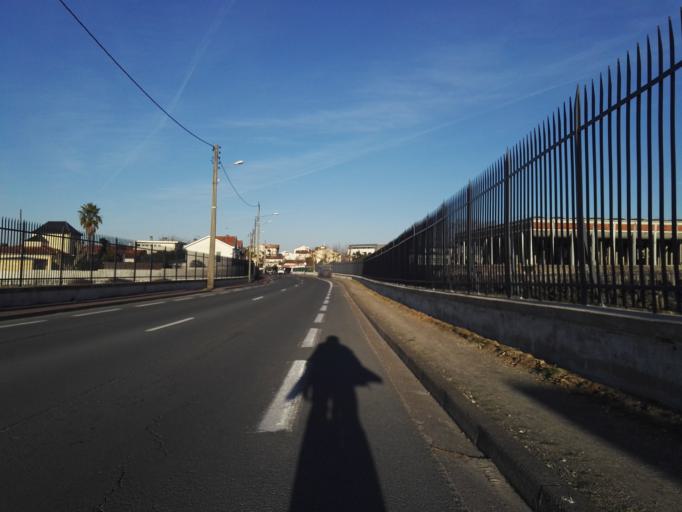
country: FR
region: Aquitaine
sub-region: Departement de la Gironde
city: Talence
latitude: 44.8172
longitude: -0.6050
